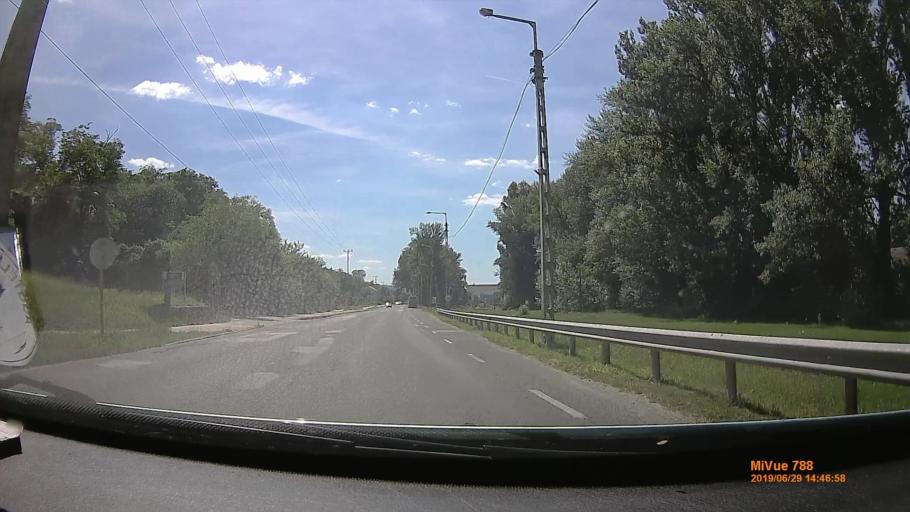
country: HU
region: Komarom-Esztergom
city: Labatlan
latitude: 47.7533
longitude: 18.5255
